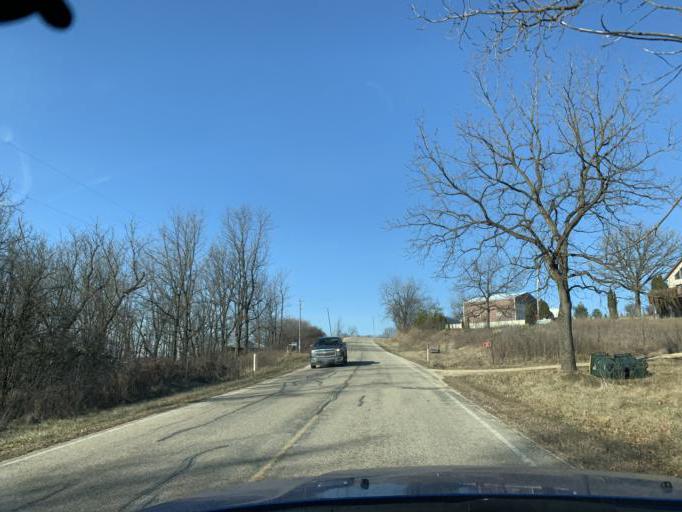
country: US
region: Wisconsin
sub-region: Iowa County
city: Barneveld
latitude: 42.8497
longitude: -89.9347
